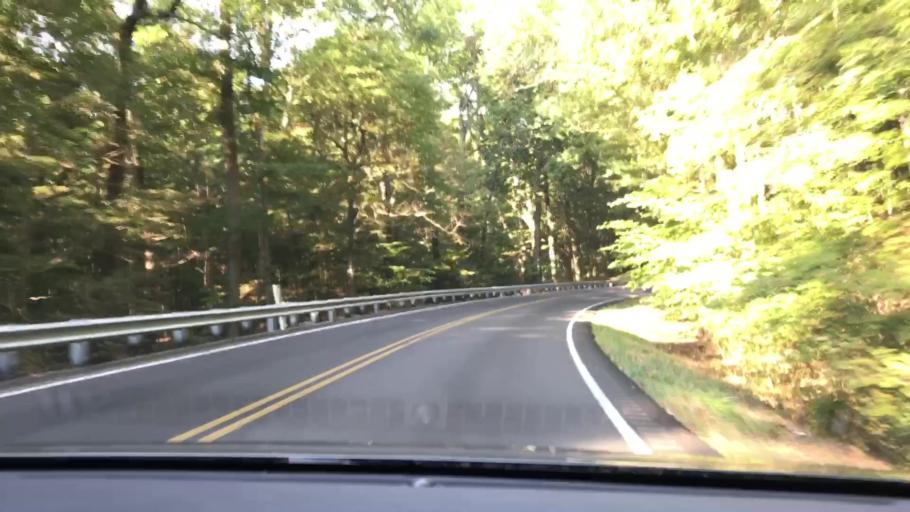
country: US
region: Kentucky
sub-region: Marshall County
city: Benton
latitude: 36.7654
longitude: -88.2695
